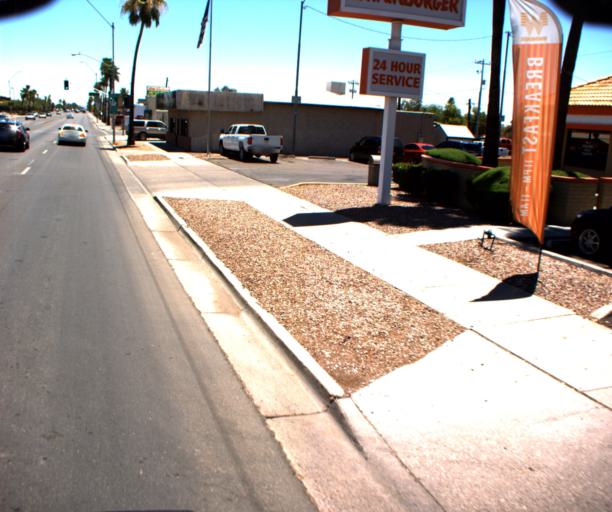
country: US
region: Arizona
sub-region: Pinal County
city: Casa Grande
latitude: 32.8795
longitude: -111.7485
